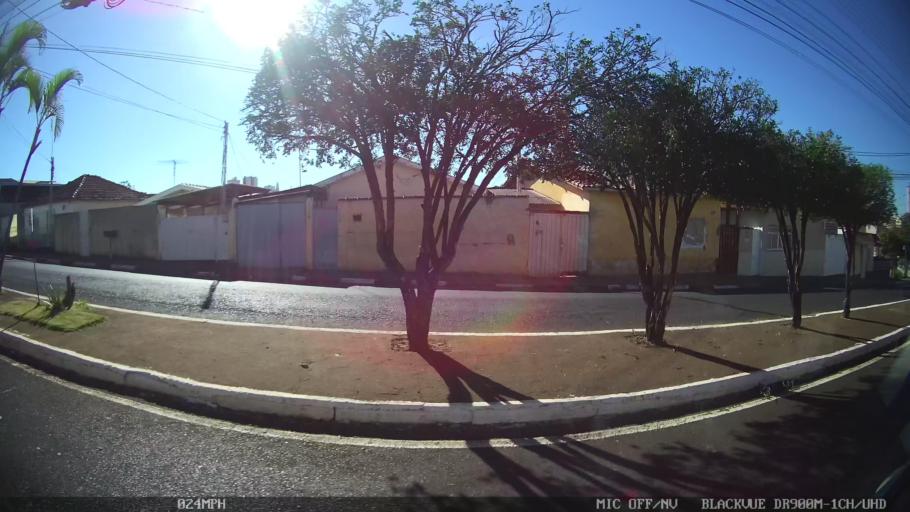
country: BR
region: Sao Paulo
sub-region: Franca
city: Franca
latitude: -20.5470
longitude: -47.4102
